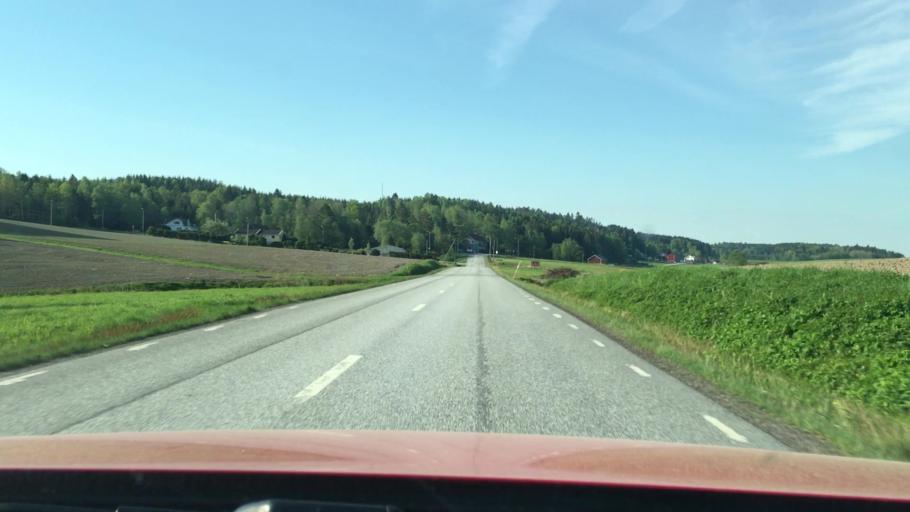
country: SE
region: Vaestra Goetaland
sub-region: Munkedals Kommun
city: Munkedal
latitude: 58.6088
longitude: 11.5589
